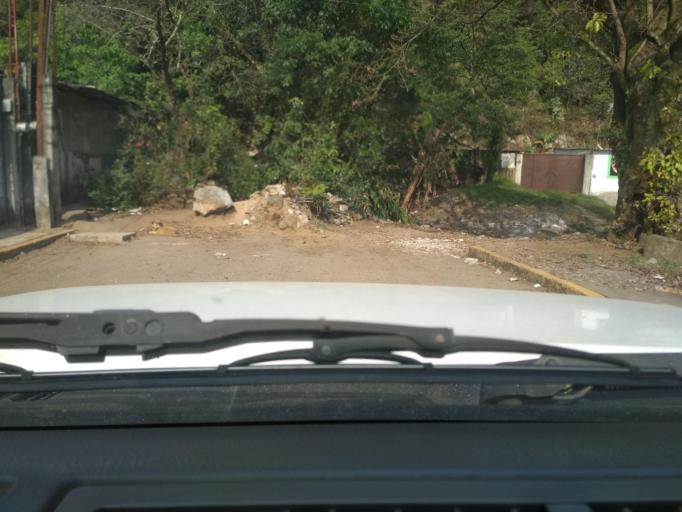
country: MX
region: Veracruz
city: Orizaba
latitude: 18.8674
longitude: -97.0940
